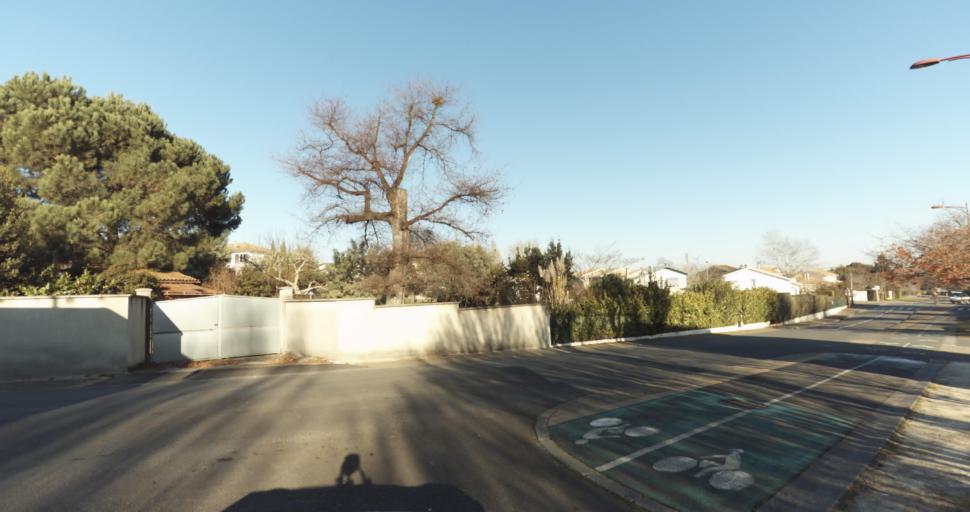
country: FR
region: Aquitaine
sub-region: Departement de la Gironde
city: Carbon-Blanc
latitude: 44.8921
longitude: -0.5074
